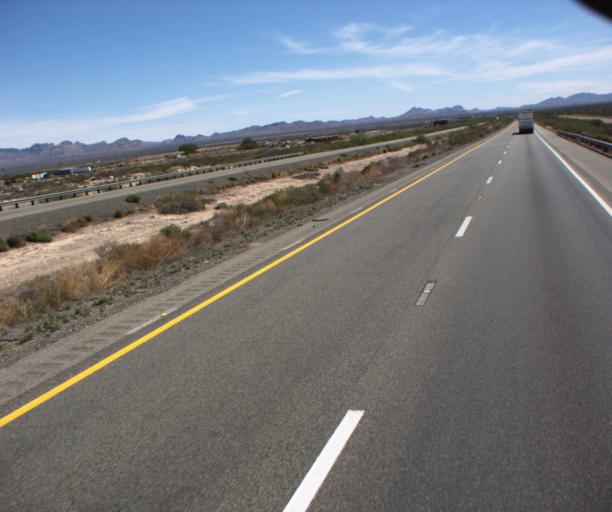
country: US
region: New Mexico
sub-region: Hidalgo County
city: Lordsburg
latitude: 32.2625
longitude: -109.2251
